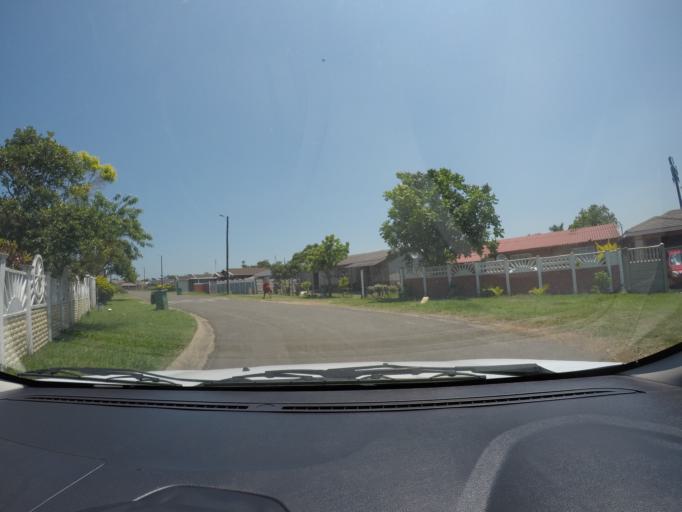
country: ZA
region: KwaZulu-Natal
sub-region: uThungulu District Municipality
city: eSikhawini
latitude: -28.8910
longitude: 31.8867
